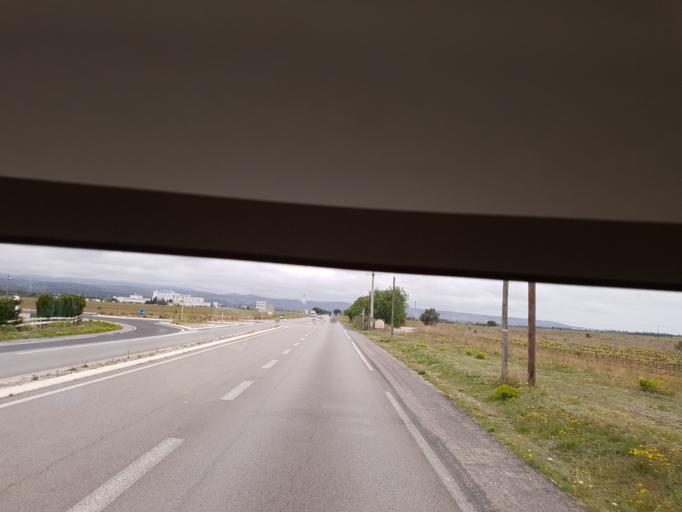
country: FR
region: Languedoc-Roussillon
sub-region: Departement des Pyrenees-Orientales
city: Salses-le-Chateau
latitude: 42.7987
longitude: 2.9096
